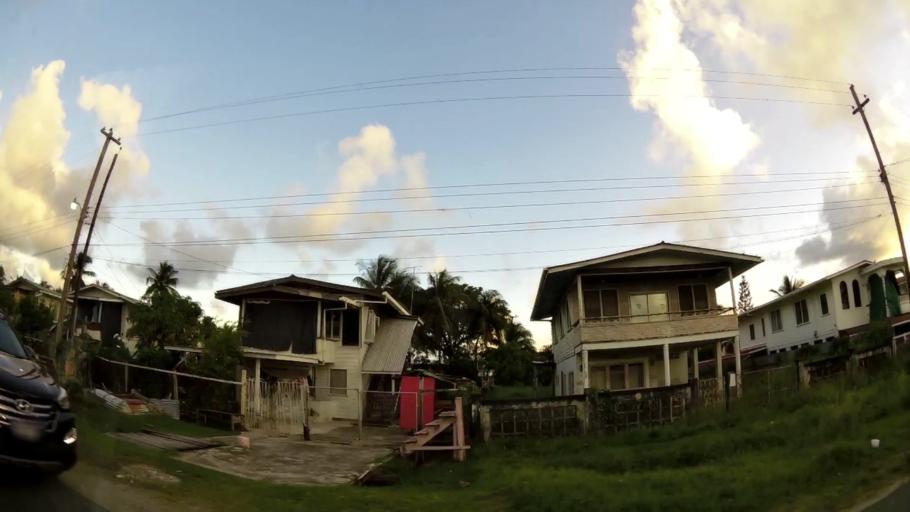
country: GY
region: Demerara-Mahaica
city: Georgetown
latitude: 6.8145
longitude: -58.1024
